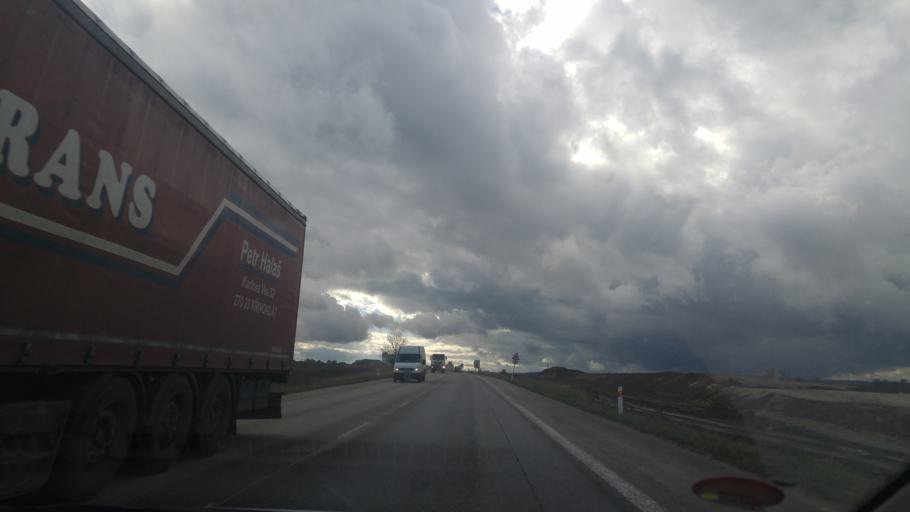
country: CZ
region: Jihocesky
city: Dolni Bukovsko
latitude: 49.1568
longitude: 14.6379
